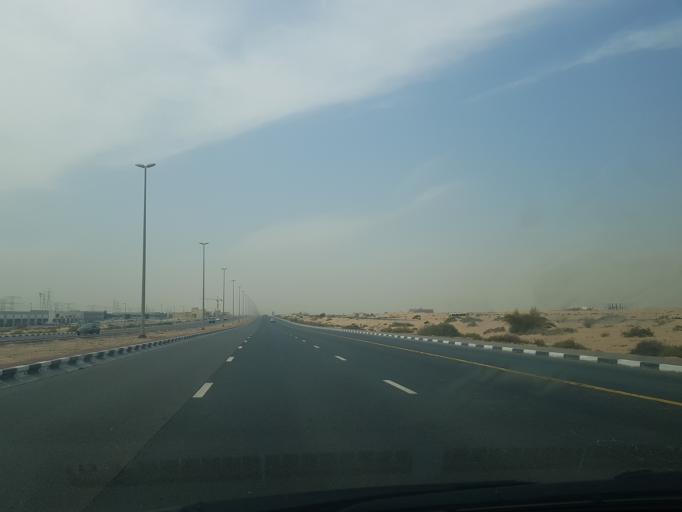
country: AE
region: Ash Shariqah
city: Sharjah
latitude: 25.2540
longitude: 55.5246
